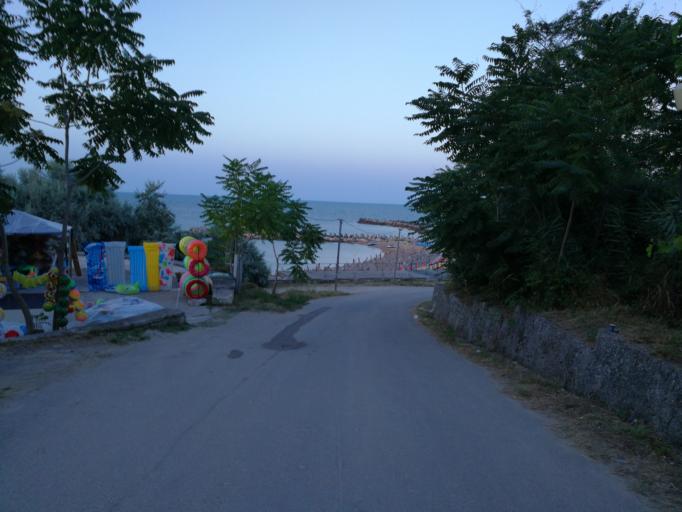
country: RO
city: Eforie Sud
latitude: 44.0278
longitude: 28.6553
